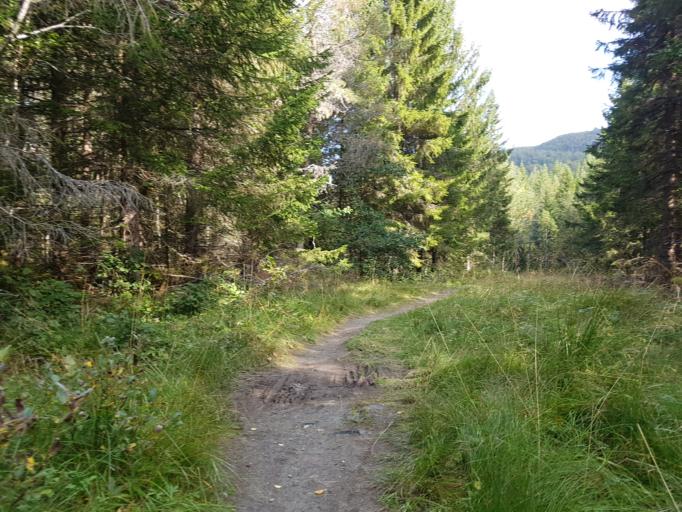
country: NO
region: Sor-Trondelag
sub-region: Trondheim
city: Trondheim
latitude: 63.4355
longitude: 10.2836
